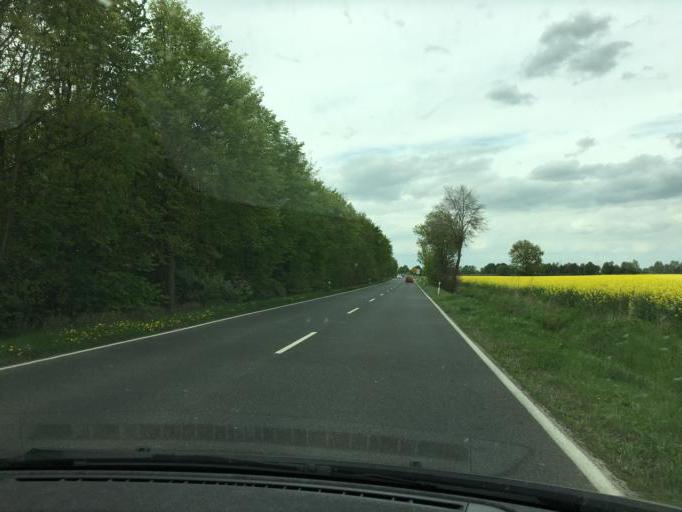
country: DE
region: North Rhine-Westphalia
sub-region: Regierungsbezirk Koln
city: Vettweiss
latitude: 50.7413
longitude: 6.6339
